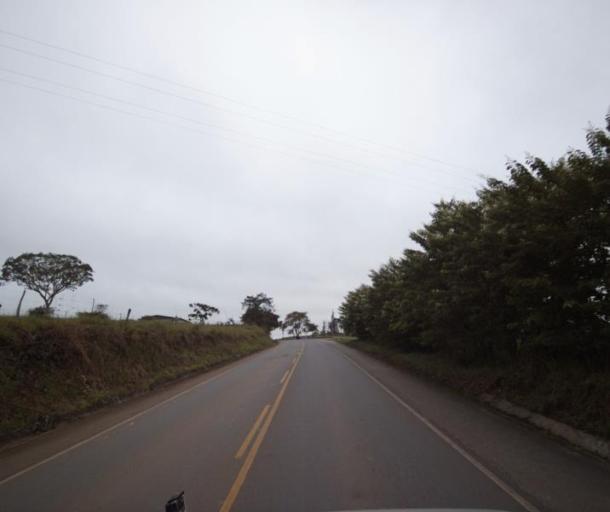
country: BR
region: Goias
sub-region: Pirenopolis
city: Pirenopolis
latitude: -15.9001
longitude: -48.7978
